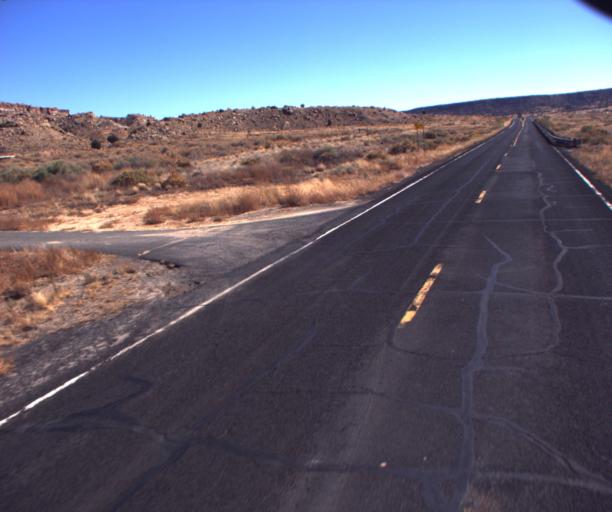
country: US
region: Arizona
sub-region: Navajo County
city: First Mesa
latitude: 35.8356
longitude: -110.2997
